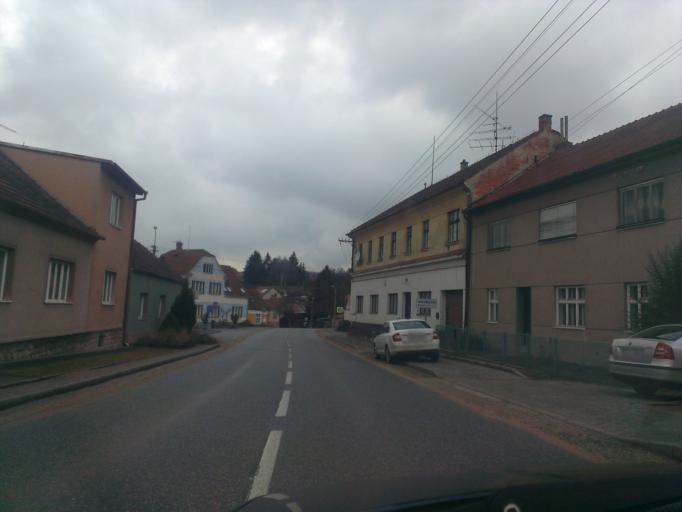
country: CZ
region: South Moravian
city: Bilovice nad Svitavou
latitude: 49.2638
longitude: 16.7152
